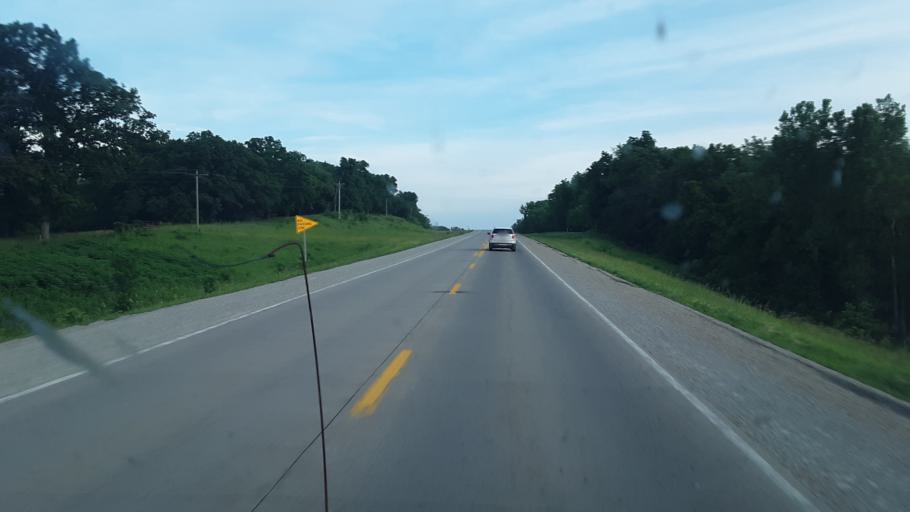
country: US
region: Iowa
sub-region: Benton County
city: Belle Plaine
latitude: 41.8391
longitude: -92.2786
